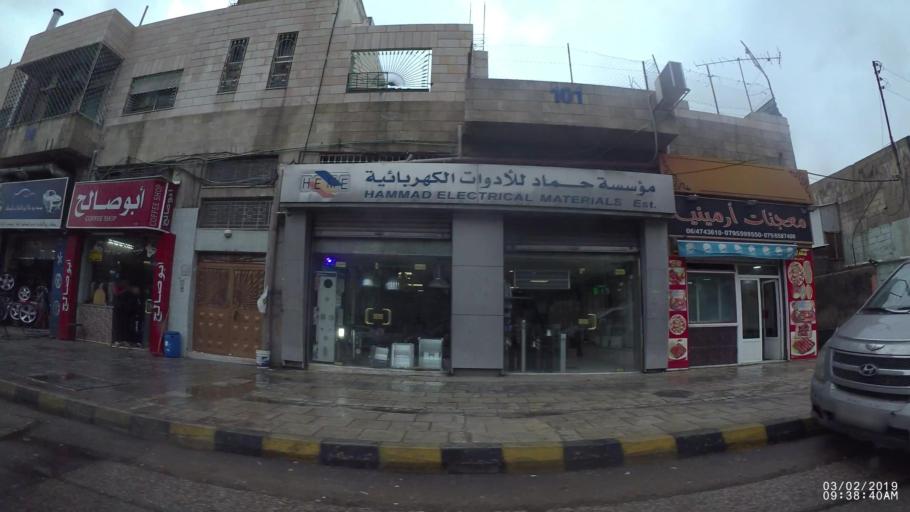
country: JO
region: Amman
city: Amman
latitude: 31.9451
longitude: 35.9186
